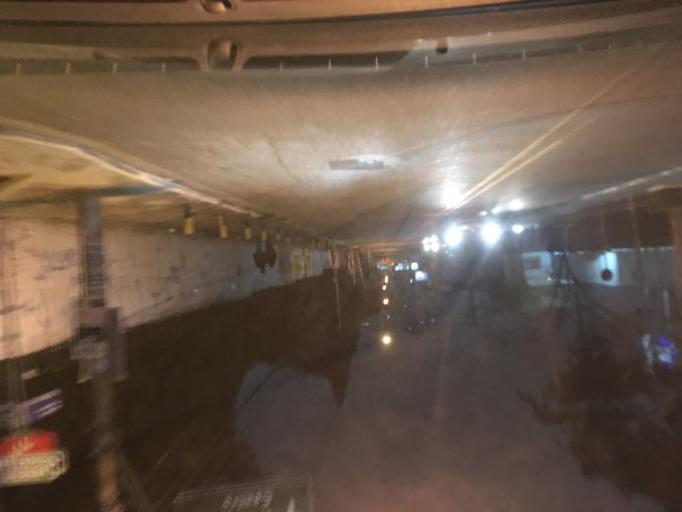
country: BR
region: Sao Paulo
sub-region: Guarulhos
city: Guarulhos
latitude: -23.4953
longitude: -46.5486
